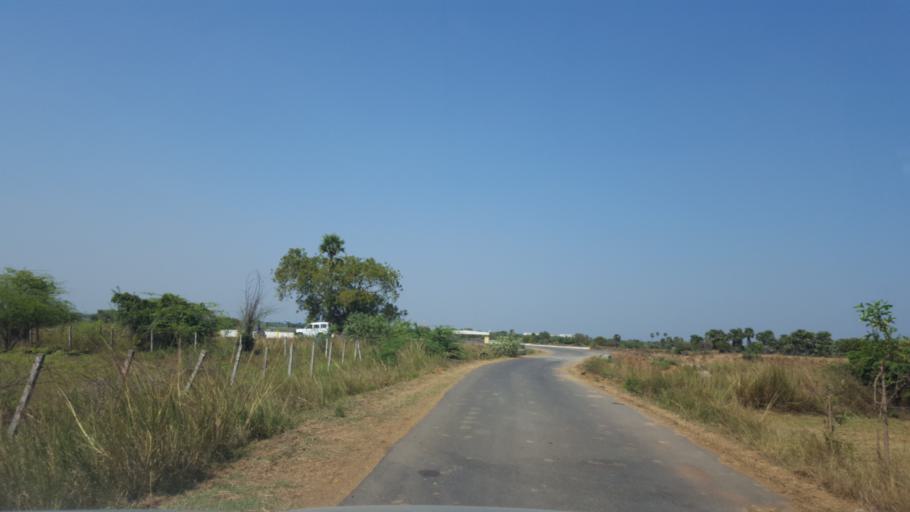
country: IN
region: Tamil Nadu
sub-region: Kancheepuram
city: Wallajahbad
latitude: 12.8586
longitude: 79.7922
